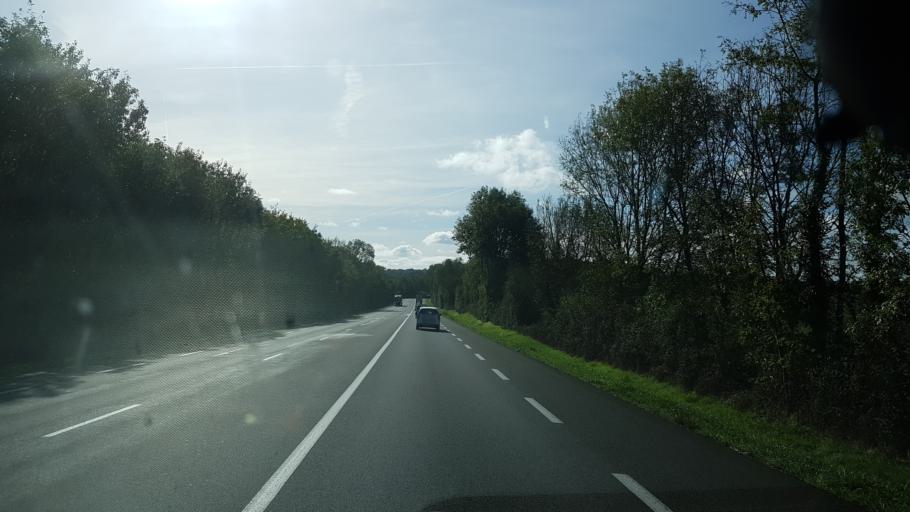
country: FR
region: Poitou-Charentes
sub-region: Departement de la Charente
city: Saint-Claud
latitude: 45.9216
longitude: 0.5152
